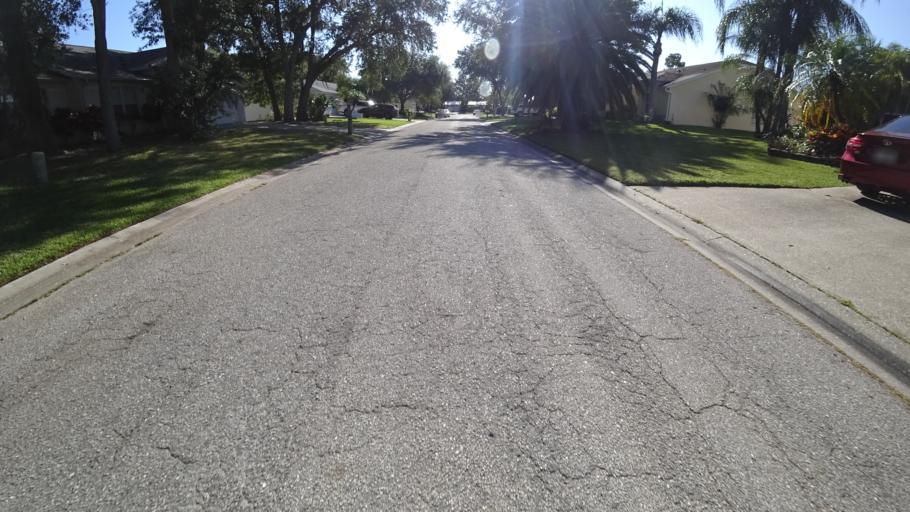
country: US
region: Florida
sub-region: Manatee County
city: Ellenton
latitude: 27.5009
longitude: -82.5102
